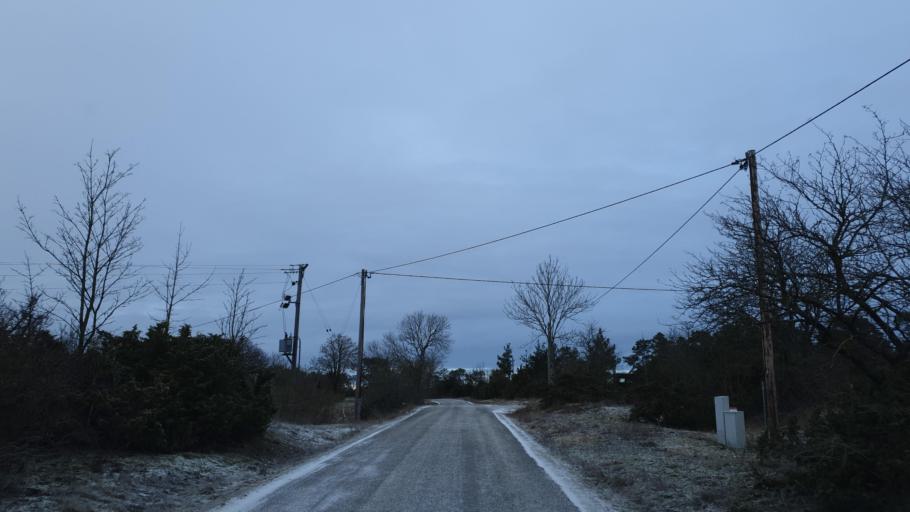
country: SE
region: Gotland
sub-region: Gotland
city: Slite
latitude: 57.3900
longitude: 18.8089
